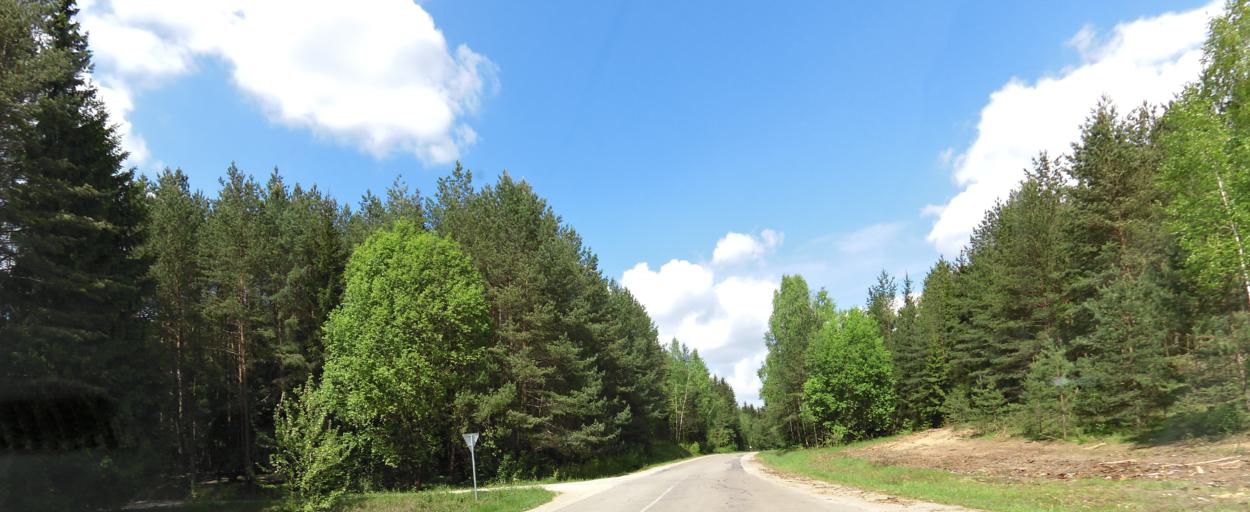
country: LT
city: Trakai
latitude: 54.7034
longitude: 24.9671
